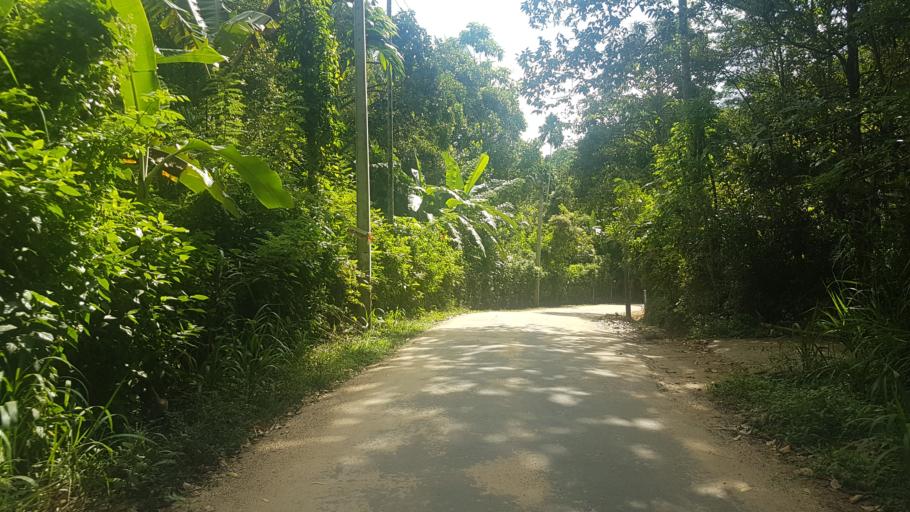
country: LK
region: Central
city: Gampola
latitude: 7.2192
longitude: 80.5866
